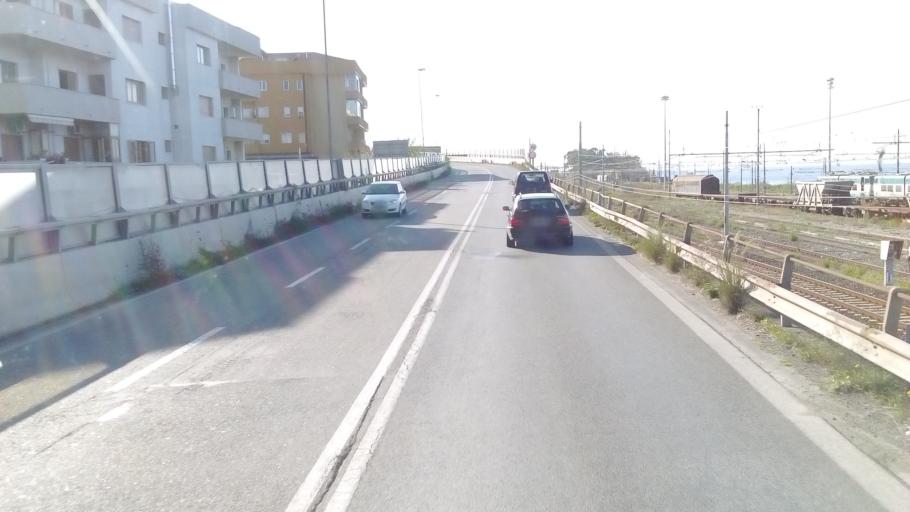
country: IT
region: Calabria
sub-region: Provincia di Reggio Calabria
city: Campo Calabro
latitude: 38.2086
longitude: 15.6354
